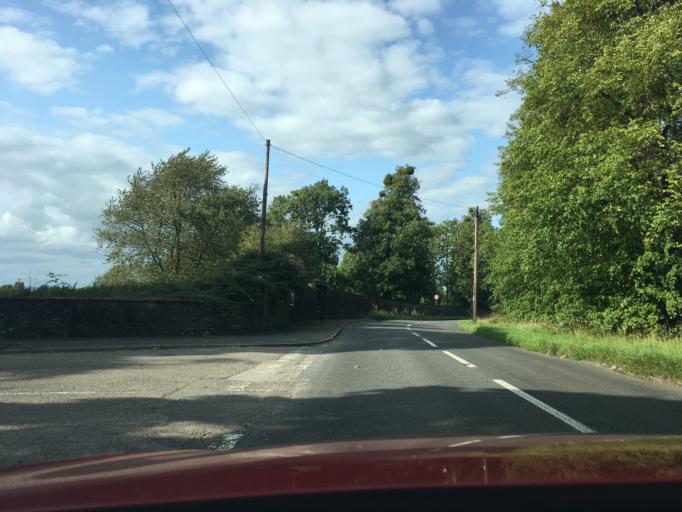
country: GB
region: England
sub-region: South Gloucestershire
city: Falfield
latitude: 51.6231
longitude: -2.4384
